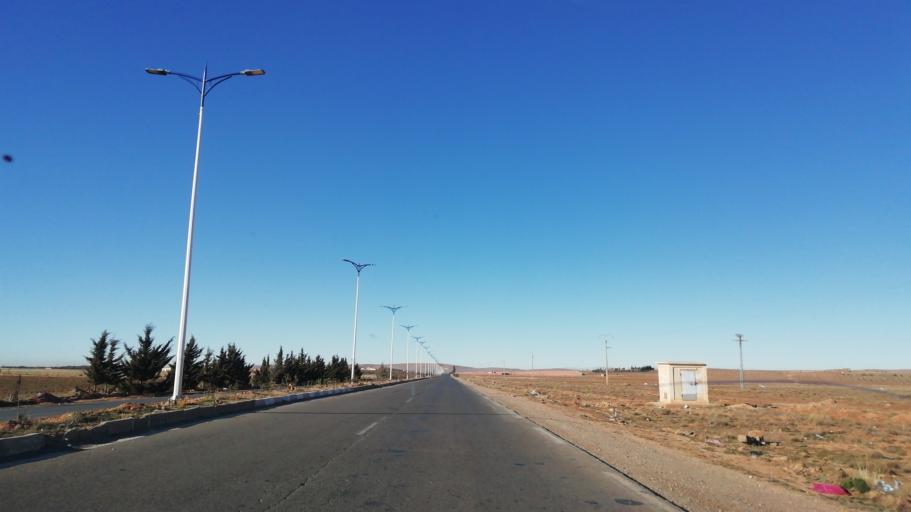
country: DZ
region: El Bayadh
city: El Bayadh
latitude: 33.6900
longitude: 1.0680
